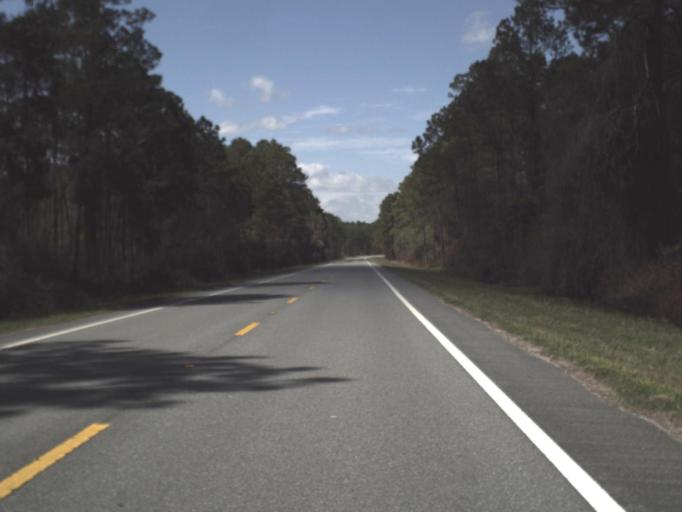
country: US
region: Florida
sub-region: Gadsden County
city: Midway
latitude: 30.3560
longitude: -84.5249
